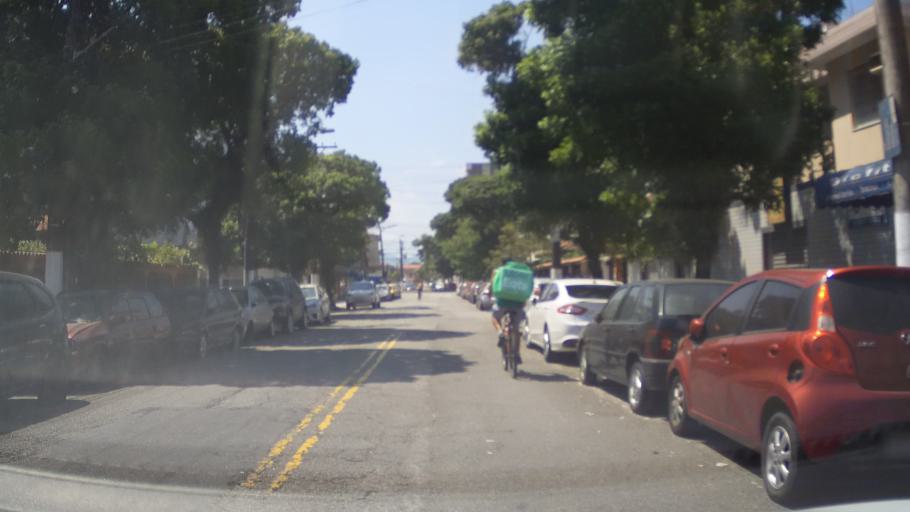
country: BR
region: Sao Paulo
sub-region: Santos
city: Santos
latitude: -23.9703
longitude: -46.3052
